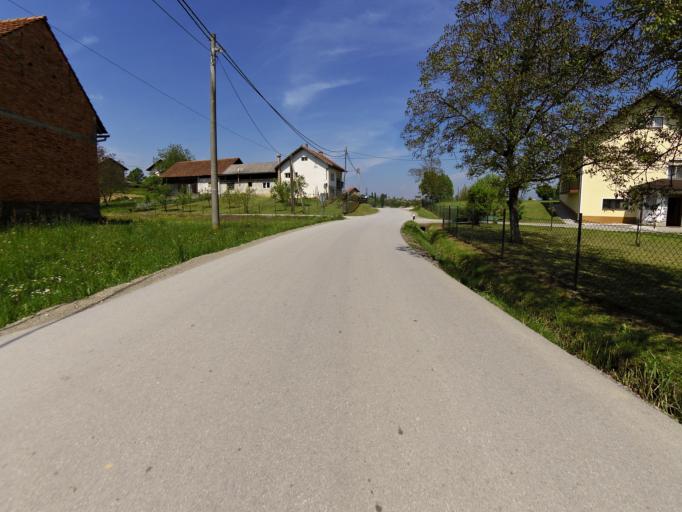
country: HR
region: Karlovacka
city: Ozalj
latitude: 45.5589
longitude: 15.4794
